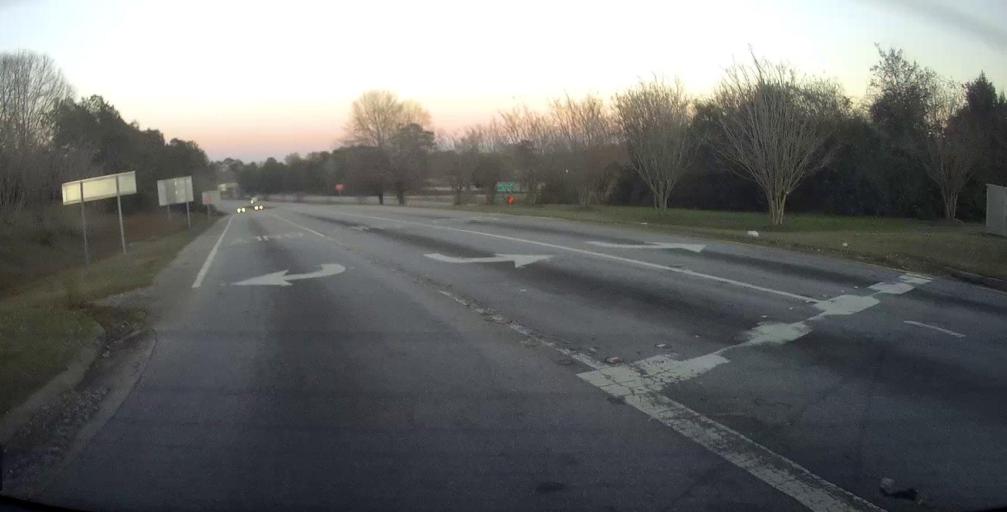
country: US
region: Alabama
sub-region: Russell County
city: Phenix City
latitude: 32.5000
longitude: -85.0178
